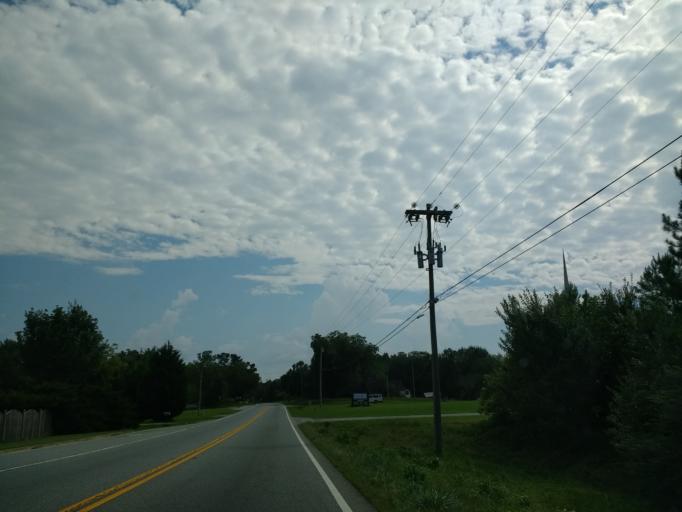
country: US
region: Georgia
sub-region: Hall County
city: Gainesville
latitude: 34.3919
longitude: -83.8048
